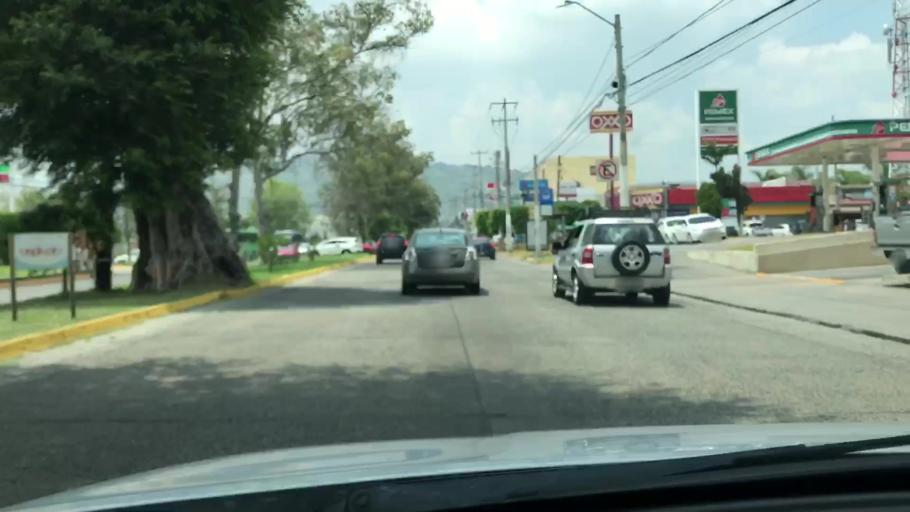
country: MX
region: Jalisco
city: Guadalajara
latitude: 20.6587
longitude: -103.4345
